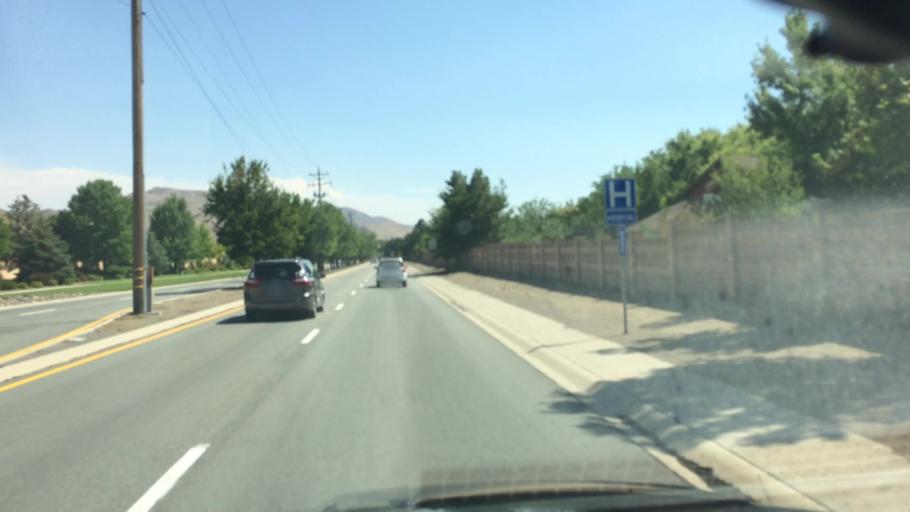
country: US
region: Nevada
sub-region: Washoe County
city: Sparks
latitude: 39.5484
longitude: -119.7059
